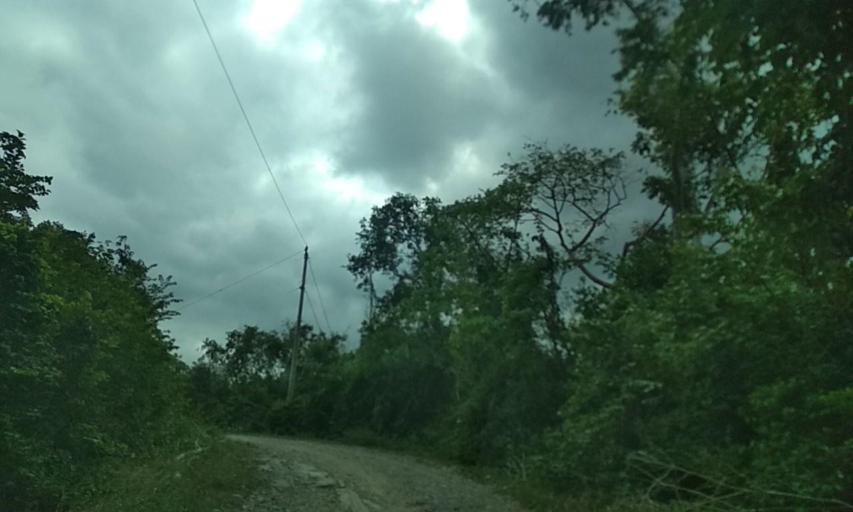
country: MX
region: Veracruz
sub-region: Papantla
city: Polutla
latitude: 20.5315
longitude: -97.2985
